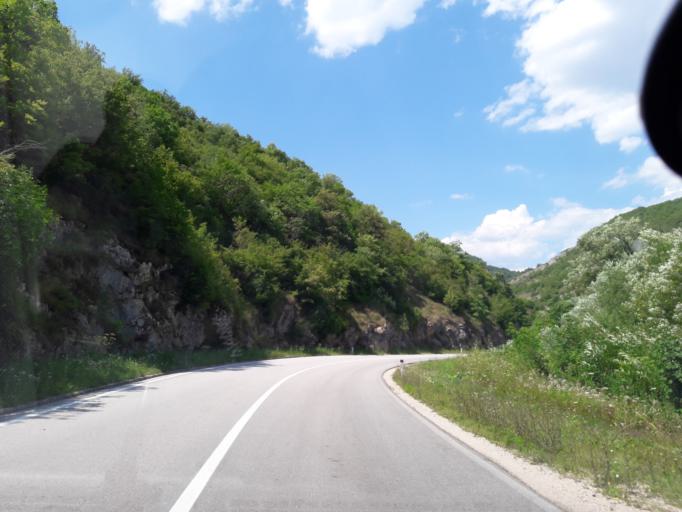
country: BA
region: Republika Srpska
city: Mrkonjic Grad
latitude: 44.4498
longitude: 17.1631
